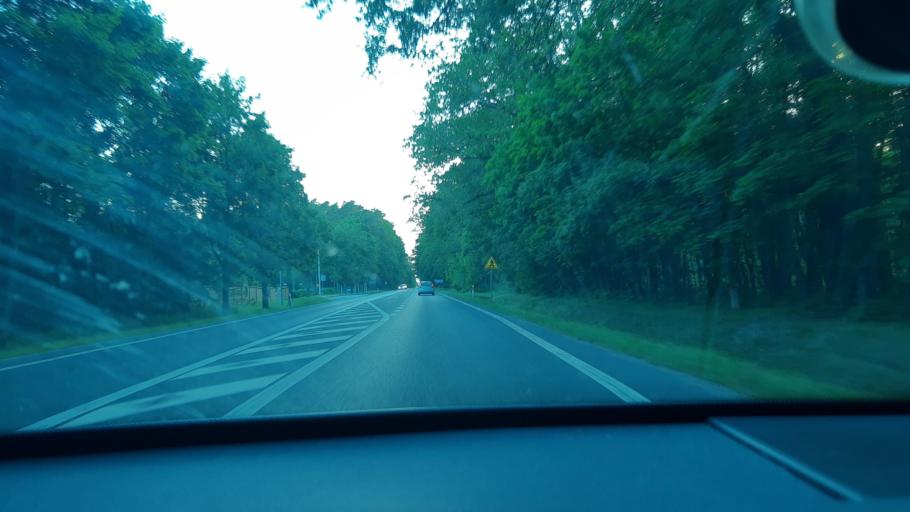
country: PL
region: Lodz Voivodeship
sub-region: Powiat zdunskowolski
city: Zapolice
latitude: 51.6039
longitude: 18.8295
